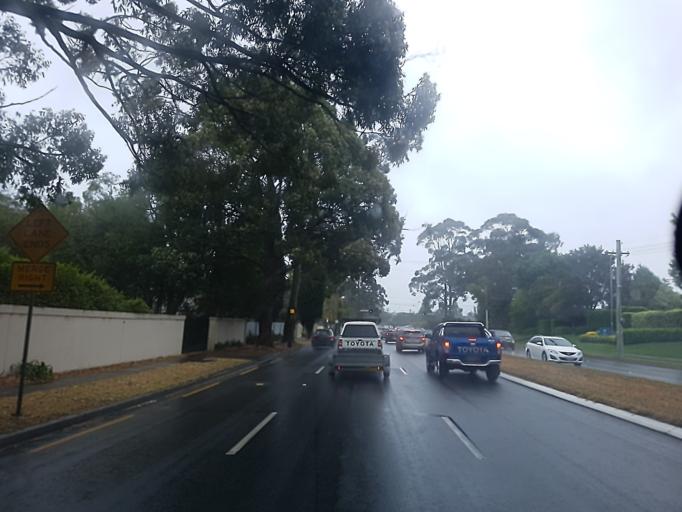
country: AU
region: New South Wales
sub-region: City of Sydney
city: North Turramurra
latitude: -33.7144
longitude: 151.1741
